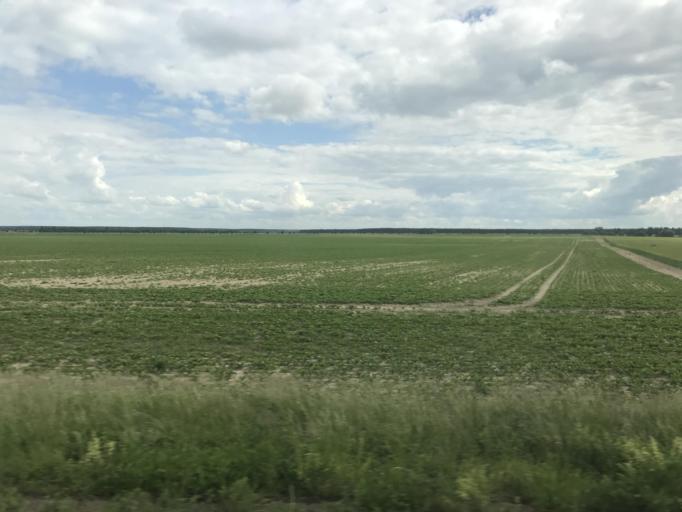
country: DE
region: Brandenburg
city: Niedergorsdorf
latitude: 51.9648
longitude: 12.9528
